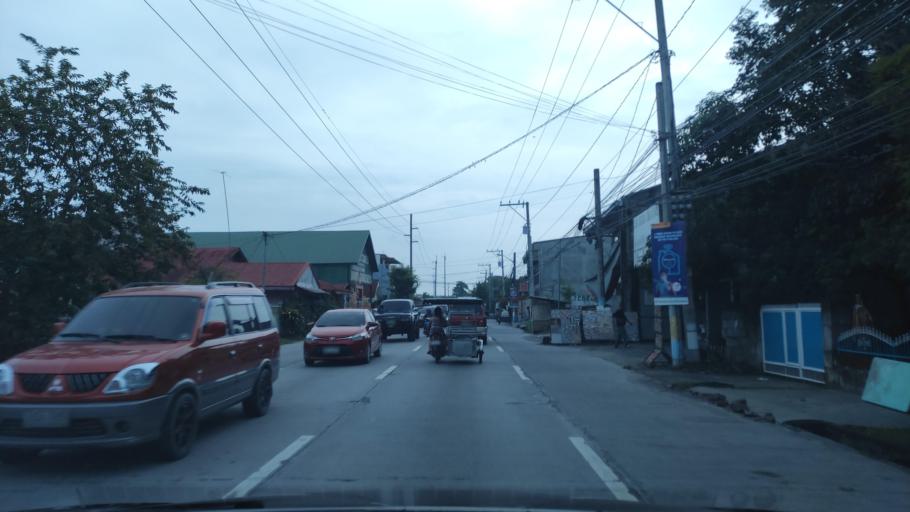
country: PH
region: Central Luzon
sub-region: Province of Pampanga
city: Santa Ana
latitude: 15.0984
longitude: 120.7683
